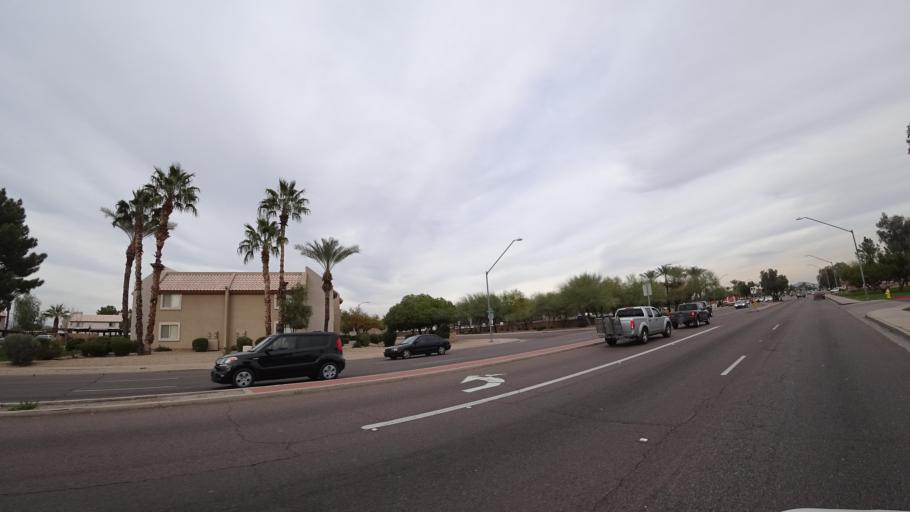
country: US
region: Arizona
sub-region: Maricopa County
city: Glendale
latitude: 33.5818
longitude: -112.1900
